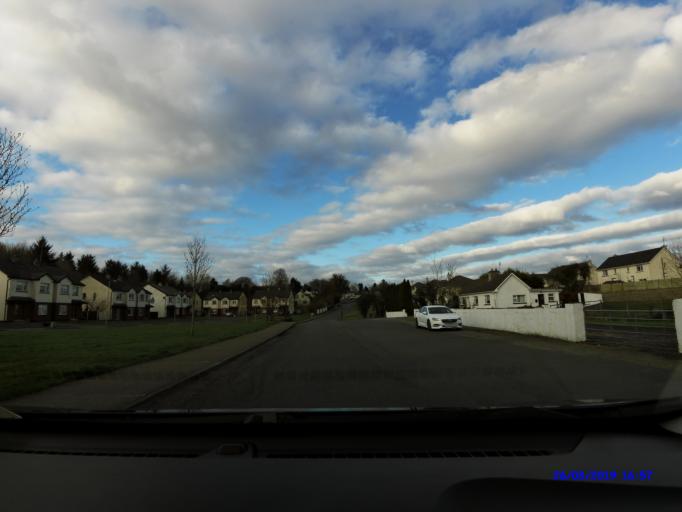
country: IE
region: Connaught
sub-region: Maigh Eo
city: Ballyhaunis
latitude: 53.7625
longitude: -8.7772
